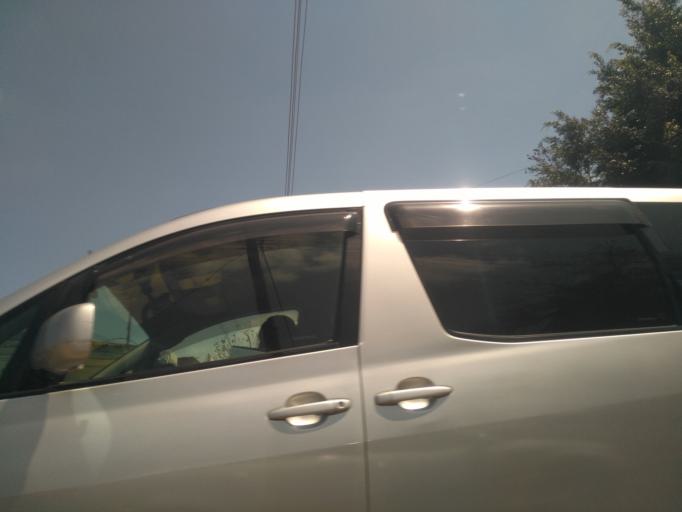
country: TZ
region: Arusha
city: Arusha
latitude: -3.3691
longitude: 36.6826
